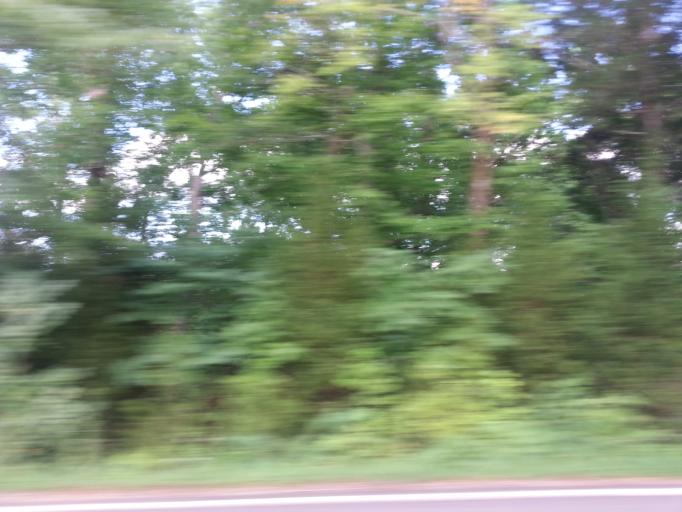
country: US
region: Tennessee
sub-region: Loudon County
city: Greenback
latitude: 35.6158
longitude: -84.0910
